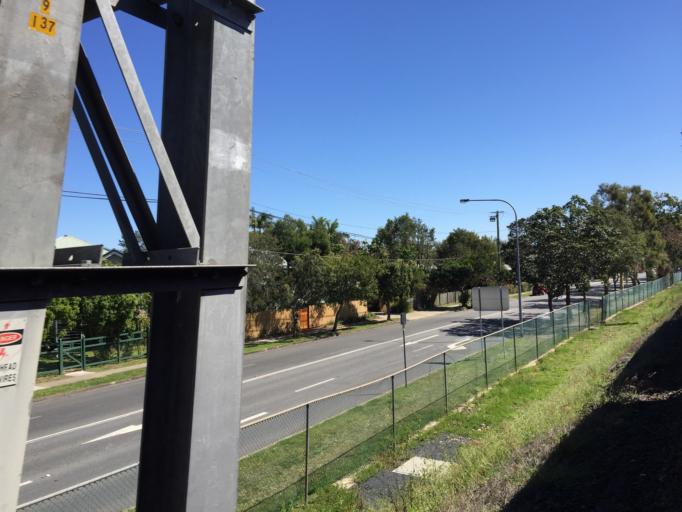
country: AU
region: Queensland
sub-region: Brisbane
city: Rocklea
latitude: -27.5242
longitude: 152.9776
